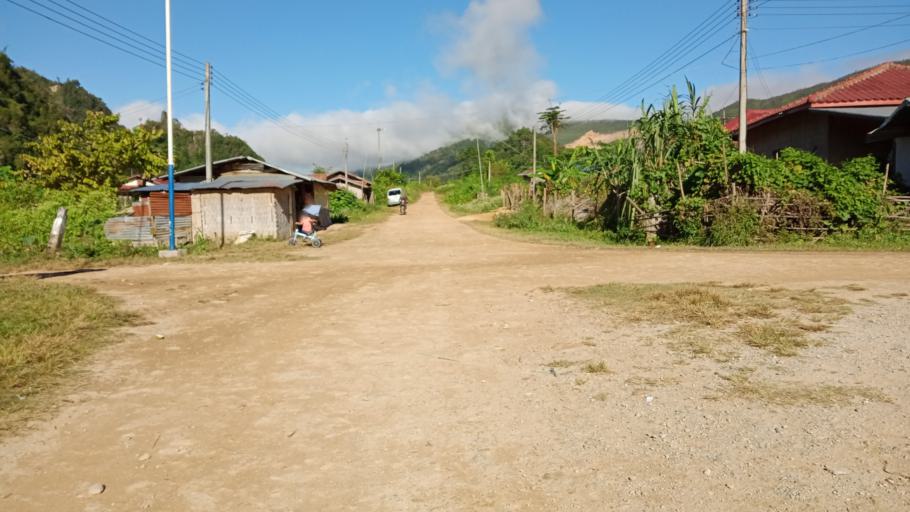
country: LA
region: Xiangkhoang
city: Phonsavan
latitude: 19.1133
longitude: 102.9144
